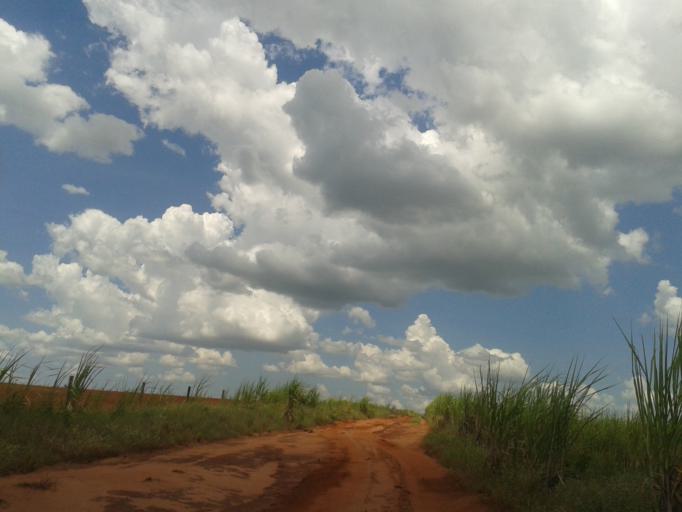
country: BR
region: Minas Gerais
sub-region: Santa Vitoria
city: Santa Vitoria
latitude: -19.1714
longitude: -50.4320
